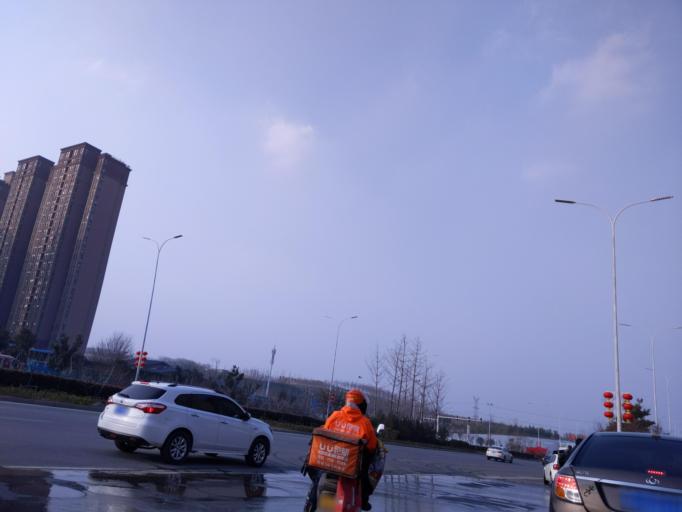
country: CN
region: Henan Sheng
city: Puyang
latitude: 35.8156
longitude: 115.0227
